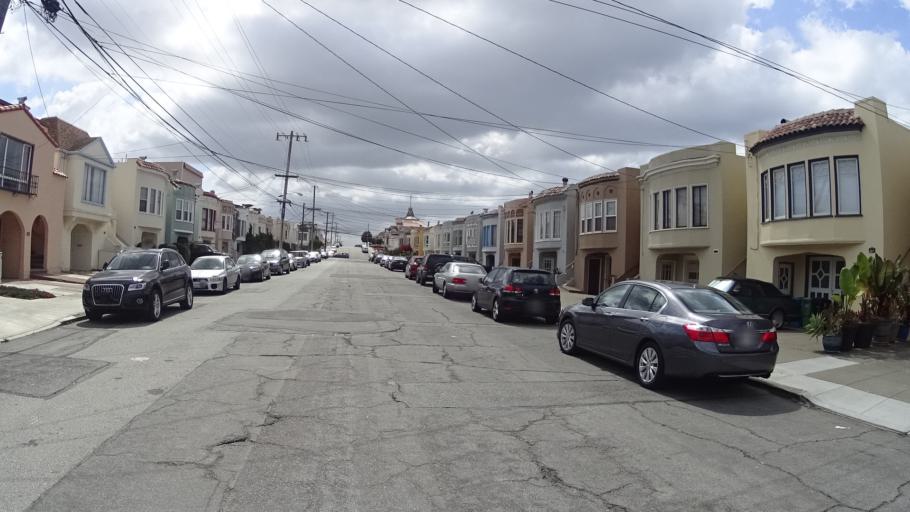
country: US
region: California
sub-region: San Mateo County
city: Daly City
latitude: 37.7601
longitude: -122.4984
